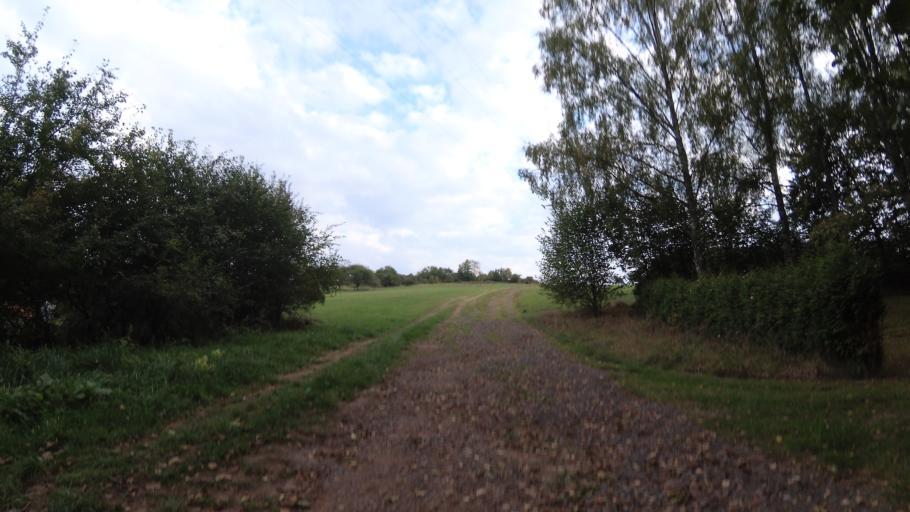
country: DE
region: Saarland
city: Ottweiler
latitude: 49.4256
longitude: 7.1501
